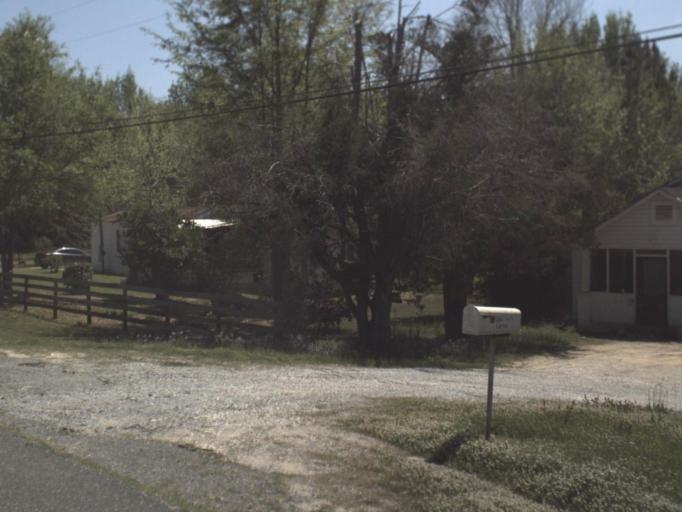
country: US
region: Florida
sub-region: Escambia County
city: Century
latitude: 30.9796
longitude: -87.2540
